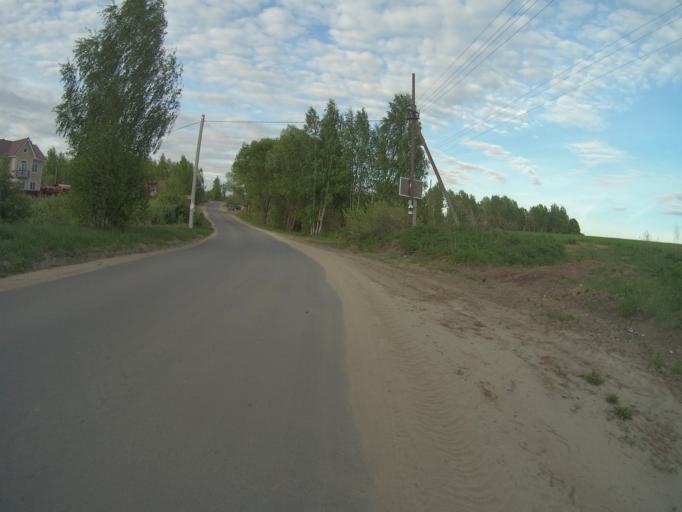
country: RU
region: Vladimir
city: Kommunar
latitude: 56.0505
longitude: 40.4825
